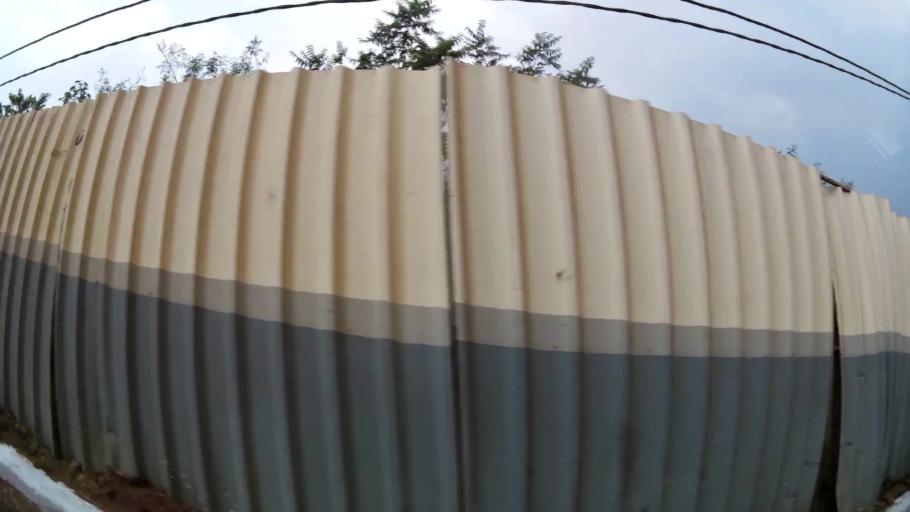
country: PY
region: Alto Parana
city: Ciudad del Este
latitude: -25.5151
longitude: -54.6066
